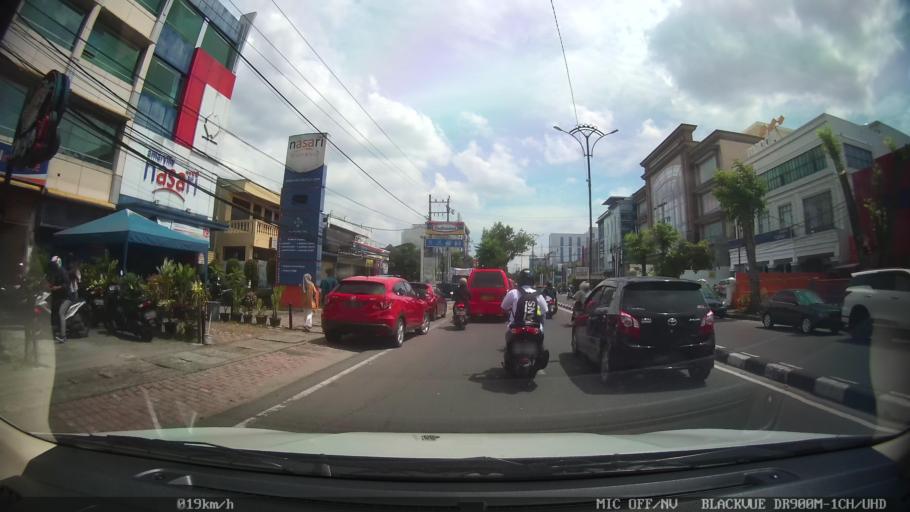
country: ID
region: North Sumatra
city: Medan
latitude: 3.5760
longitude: 98.6610
